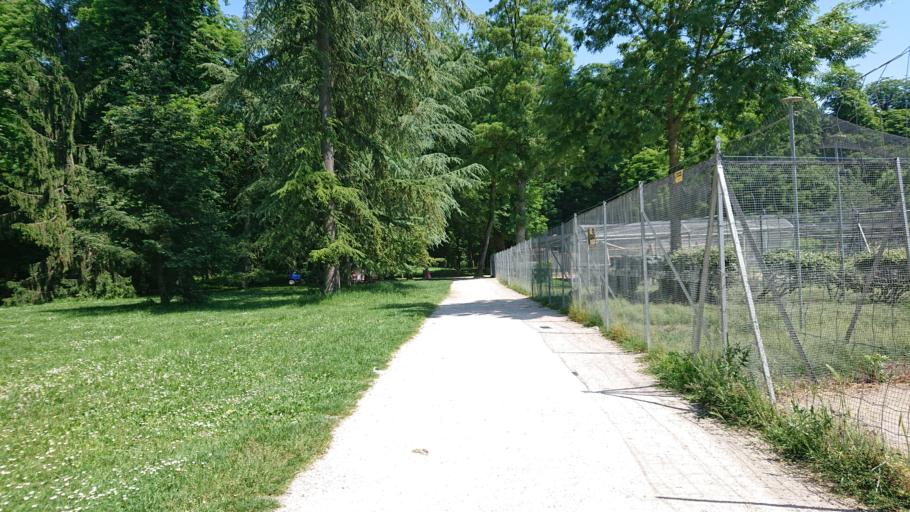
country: FR
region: Bourgogne
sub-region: Departement de la Cote-d'Or
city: Longvic
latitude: 47.2987
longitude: 5.0427
